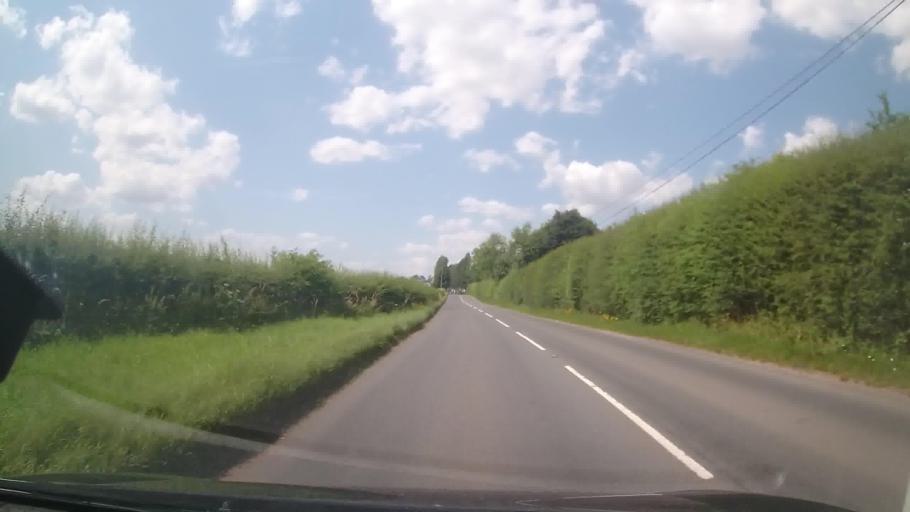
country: GB
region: England
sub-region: Herefordshire
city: Bodenham
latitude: 52.1507
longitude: -2.6457
